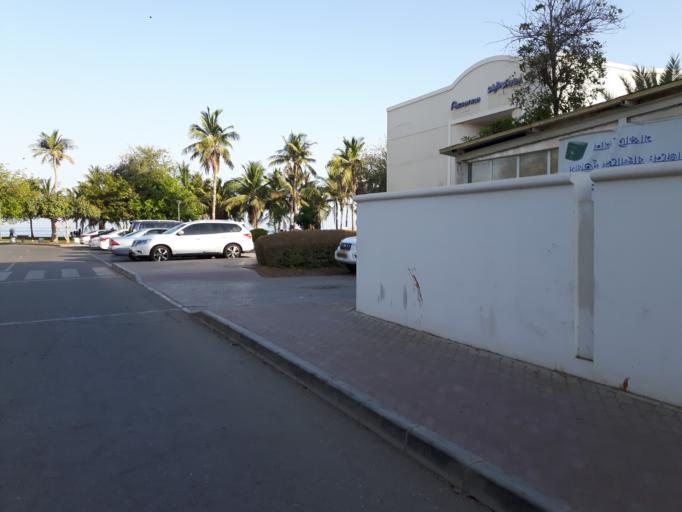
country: OM
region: Muhafazat Masqat
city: Bawshar
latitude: 23.6117
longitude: 58.4519
